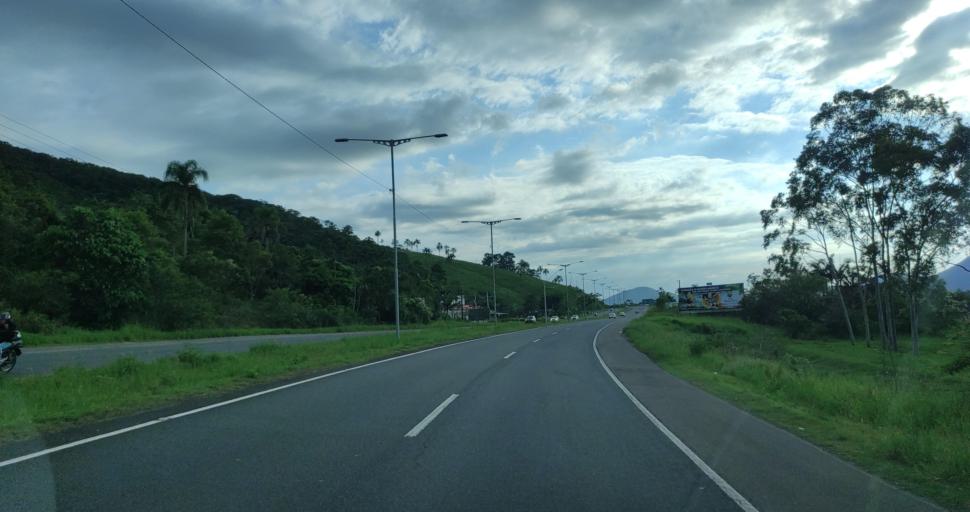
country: BR
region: Santa Catarina
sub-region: Penha
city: Penha
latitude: -26.8096
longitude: -48.6558
